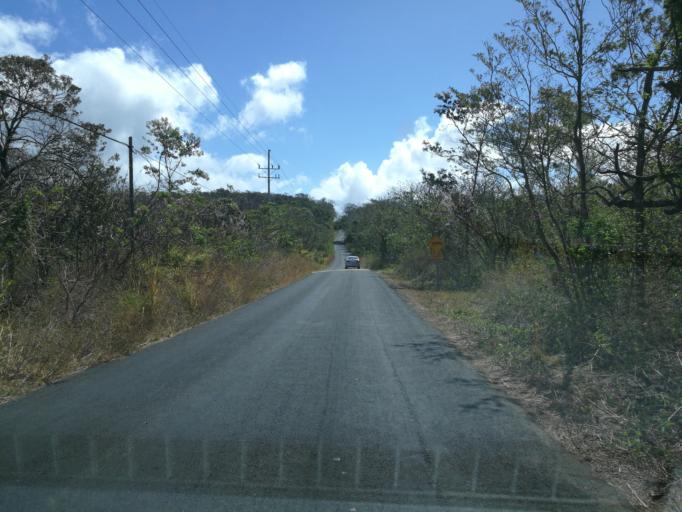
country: CR
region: Guanacaste
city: Liberia
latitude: 10.7552
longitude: -85.3720
